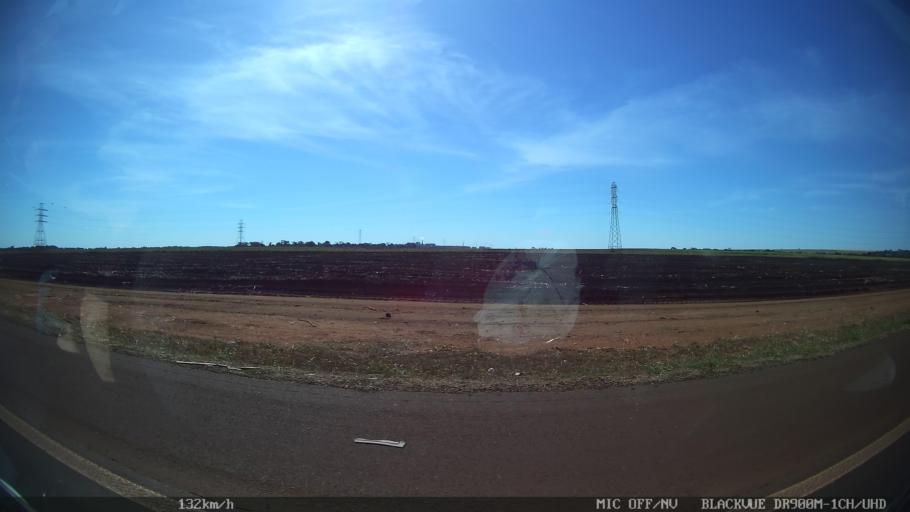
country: BR
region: Sao Paulo
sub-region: Guaira
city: Guaira
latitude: -20.4466
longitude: -48.2117
